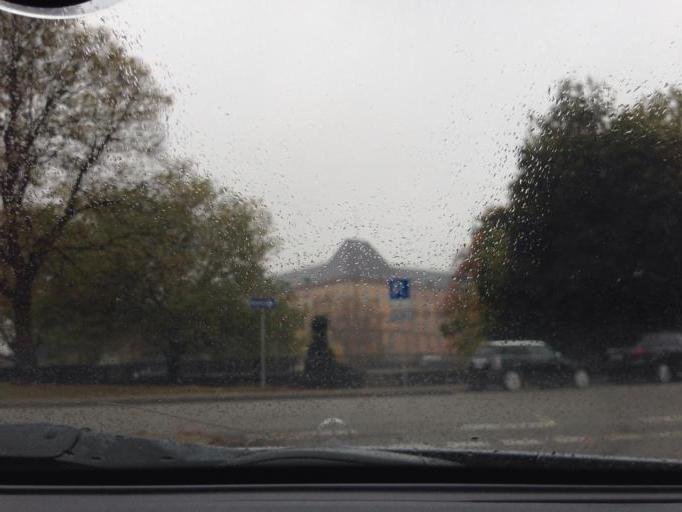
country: DE
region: Hamburg
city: Neustadt
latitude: 53.5560
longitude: 9.9797
